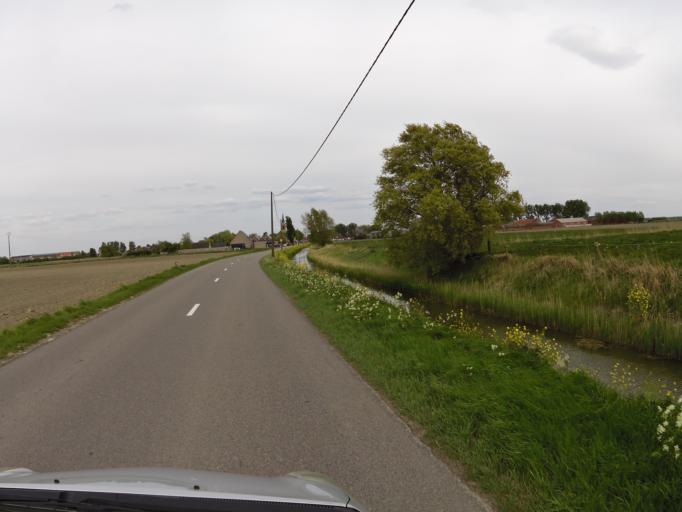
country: BE
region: Flanders
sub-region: Provincie West-Vlaanderen
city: Diksmuide
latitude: 51.0451
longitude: 2.7885
